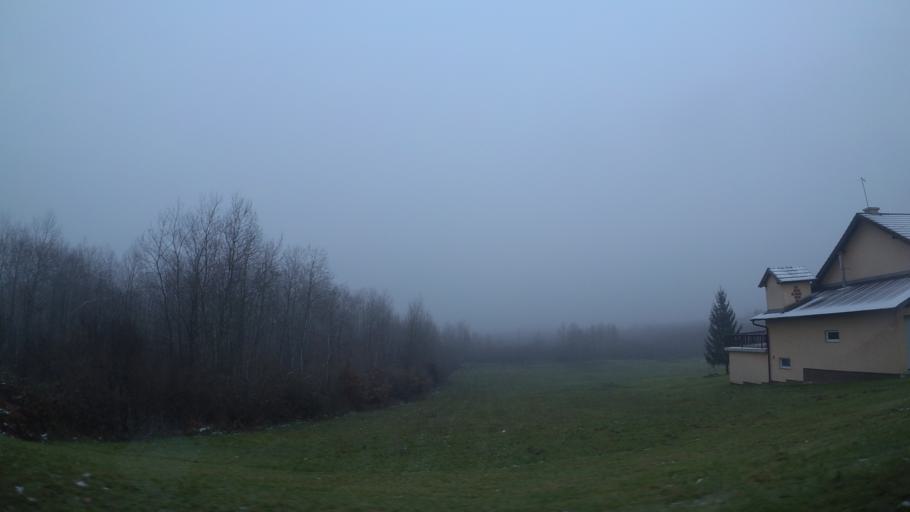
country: HR
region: Sisacko-Moslavacka
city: Glina
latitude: 45.3068
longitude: 15.9867
